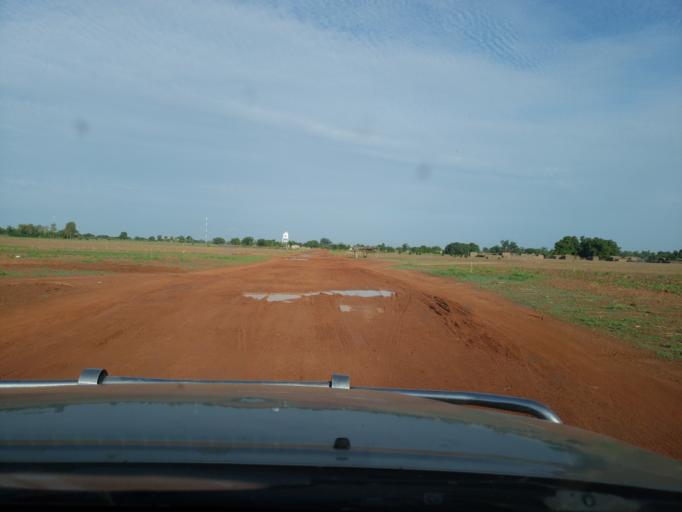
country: ML
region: Sikasso
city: Koutiala
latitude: 12.4234
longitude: -5.6723
